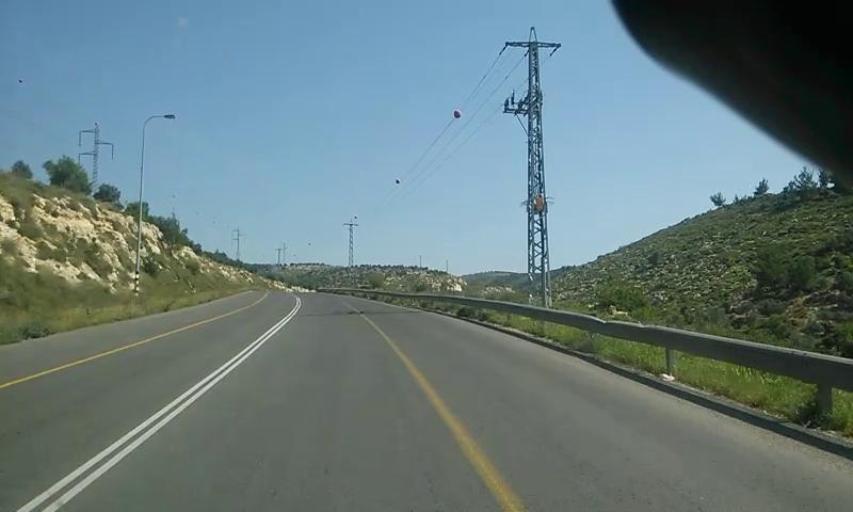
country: PS
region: West Bank
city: Idhna
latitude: 31.5671
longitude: 34.9892
